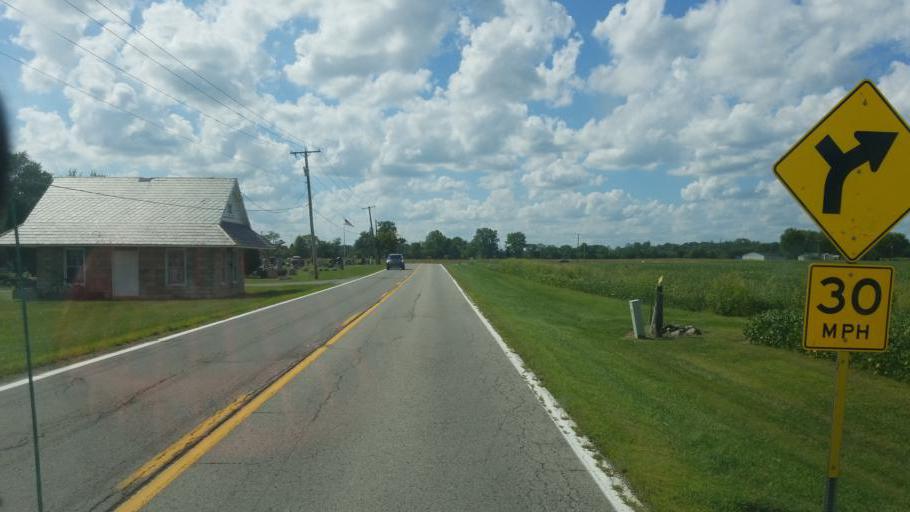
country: US
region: Ohio
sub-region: Union County
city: Richwood
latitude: 40.3964
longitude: -83.2791
